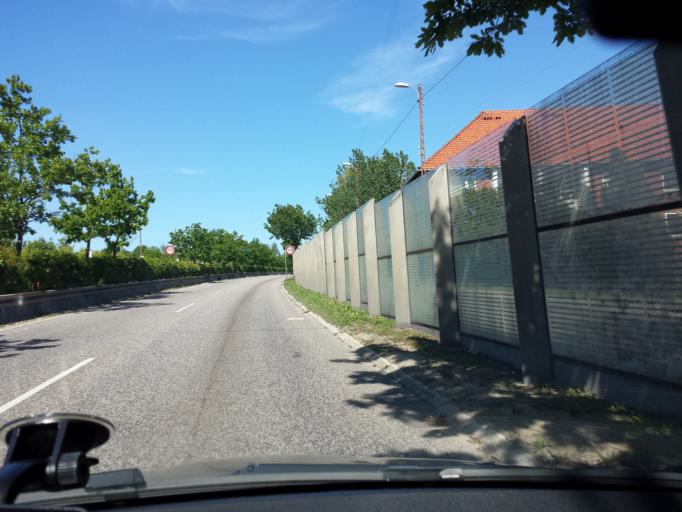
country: DK
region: Capital Region
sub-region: Herlev Kommune
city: Herlev
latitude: 55.7289
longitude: 12.4440
